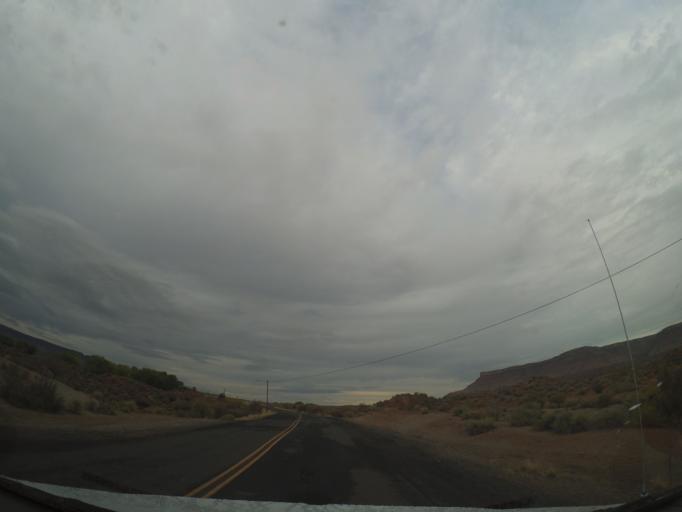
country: US
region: Utah
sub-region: Washington County
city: LaVerkin
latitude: 37.2130
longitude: -113.1719
